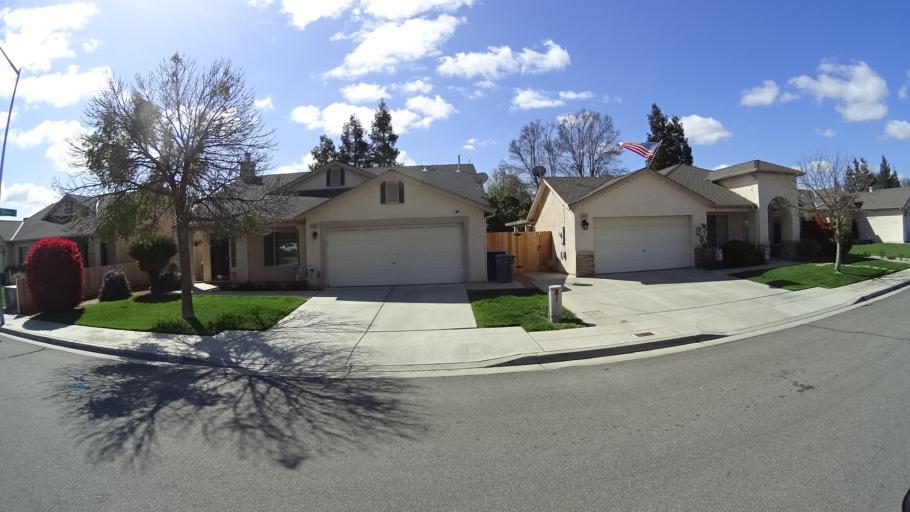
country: US
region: California
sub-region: Fresno County
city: West Park
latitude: 36.8275
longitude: -119.8770
